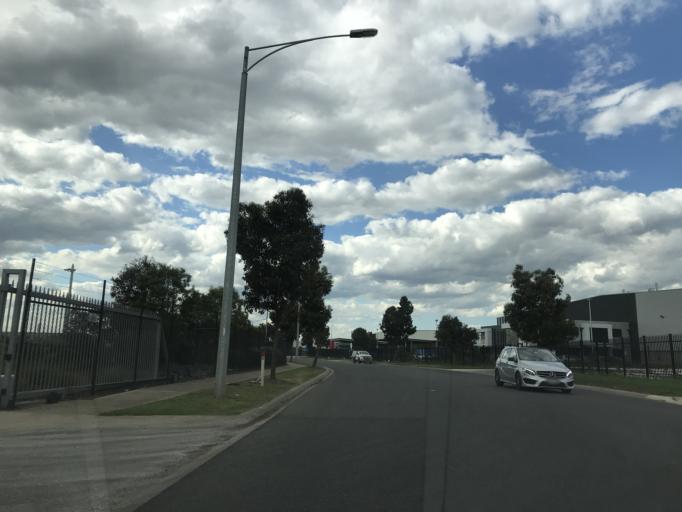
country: AU
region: Victoria
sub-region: Wyndham
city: Truganina
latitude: -37.8220
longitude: 144.7379
